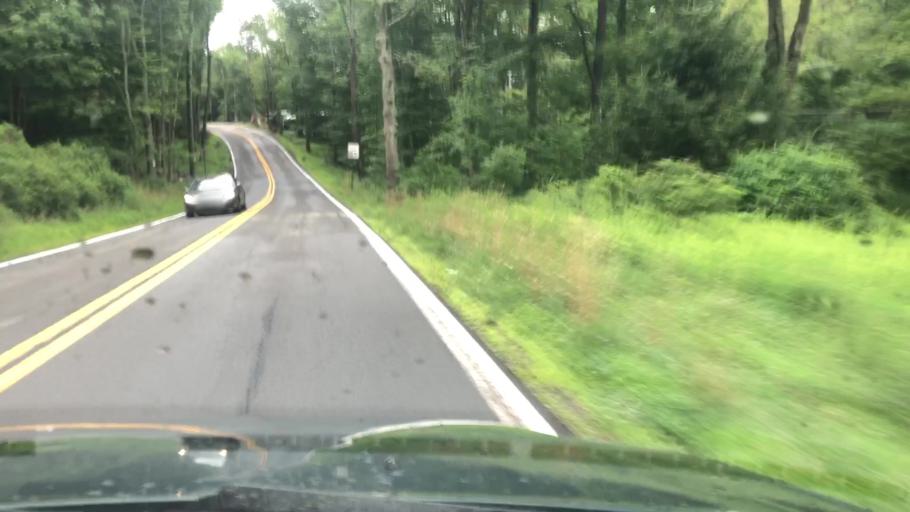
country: US
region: Pennsylvania
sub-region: Monroe County
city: Mountainhome
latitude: 41.2866
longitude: -75.2284
